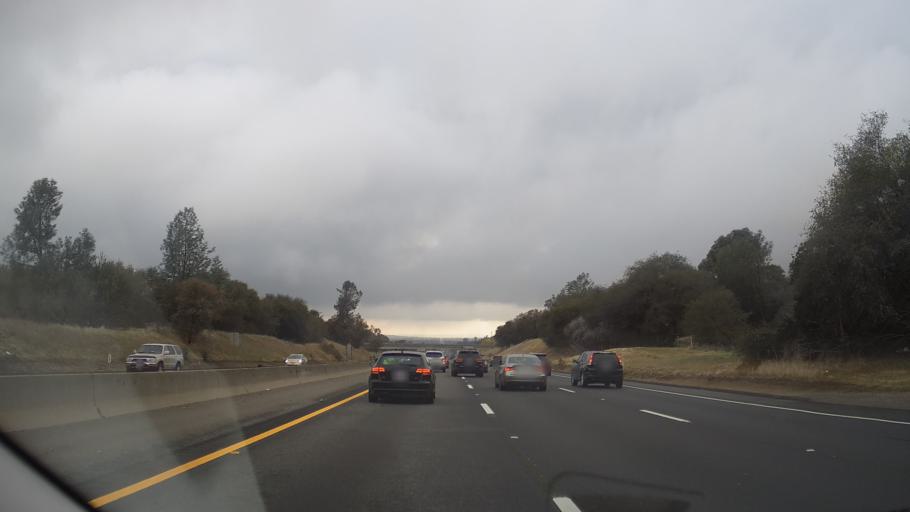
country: US
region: California
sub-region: Placer County
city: Newcastle
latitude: 38.8572
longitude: -121.1406
